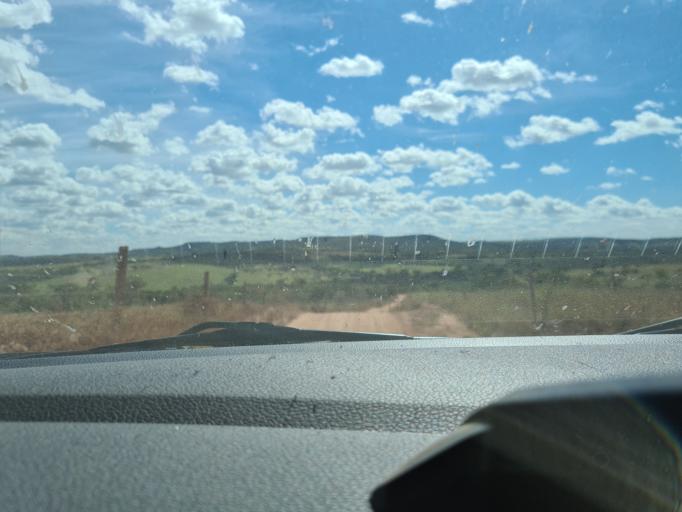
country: BR
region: Goias
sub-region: Silvania
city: Silvania
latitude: -16.5403
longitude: -48.5792
